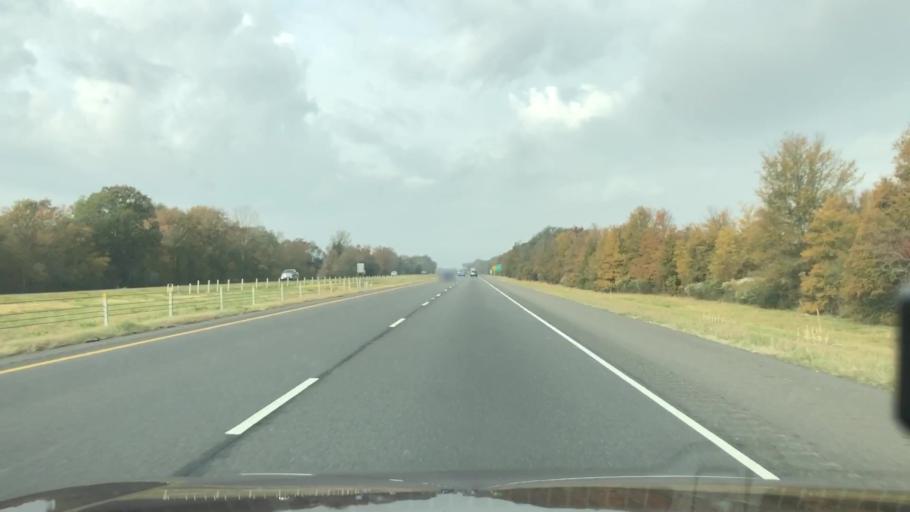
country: US
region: Louisiana
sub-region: Richland Parish
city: Delhi
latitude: 32.4540
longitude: -91.6000
